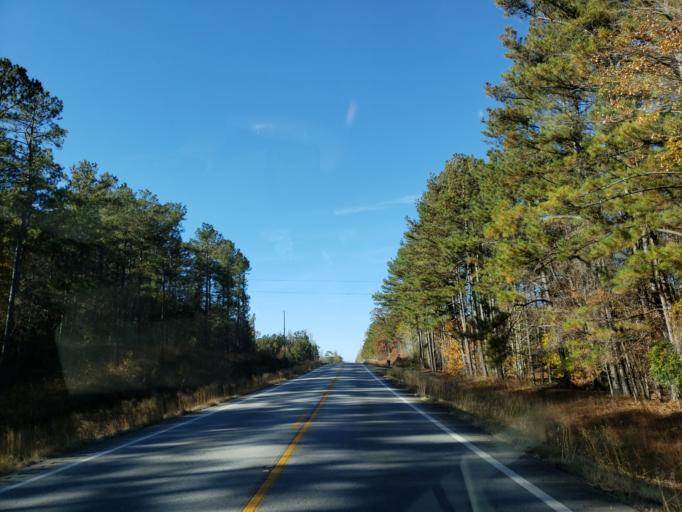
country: US
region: Alabama
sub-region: Calhoun County
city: Choccolocco
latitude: 33.5794
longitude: -85.6745
